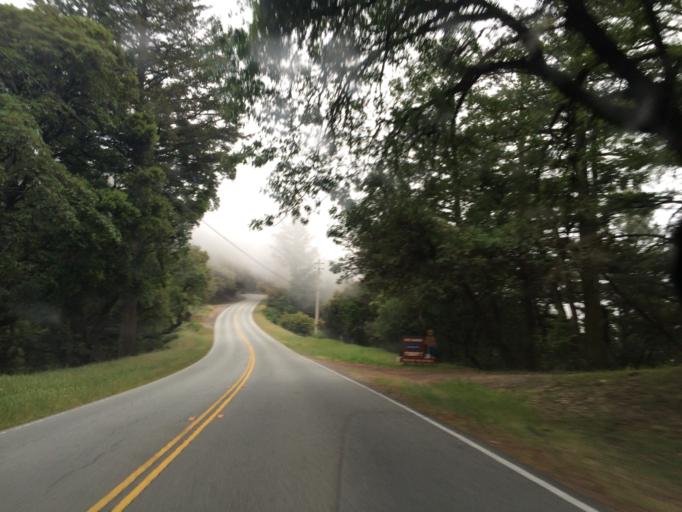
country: US
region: California
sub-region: Santa Clara County
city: Loyola
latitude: 37.2607
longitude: -122.1314
